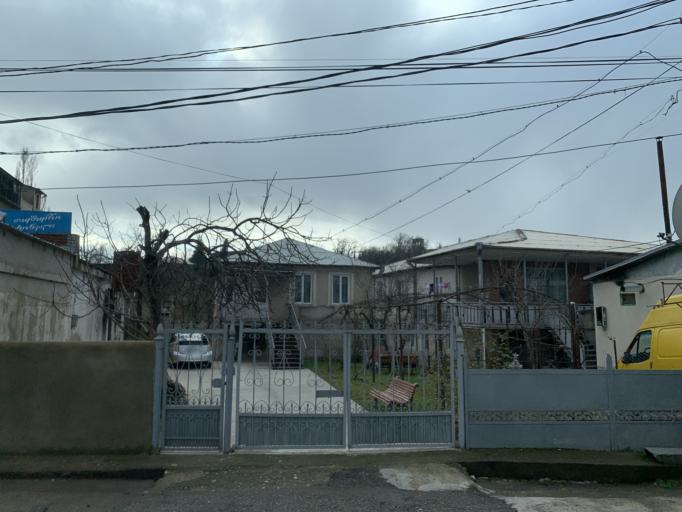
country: GE
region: Imereti
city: Tsqaltubo
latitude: 42.3298
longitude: 42.5982
